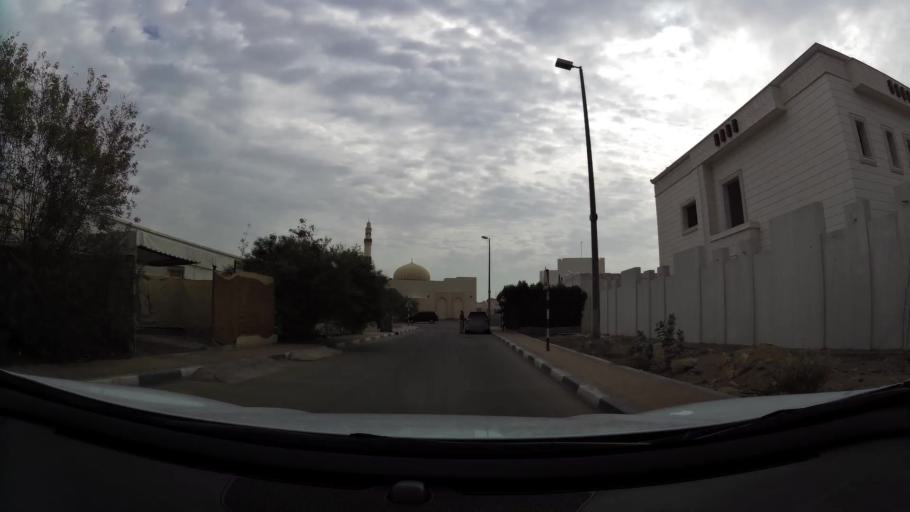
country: AE
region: Abu Dhabi
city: Al Ain
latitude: 24.2232
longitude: 55.7343
